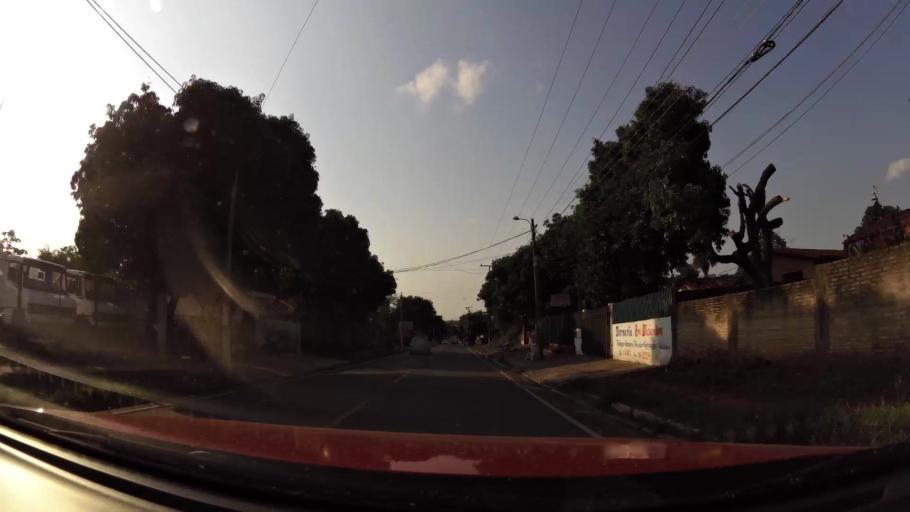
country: PY
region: Central
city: Lambare
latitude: -25.3426
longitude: -57.5900
